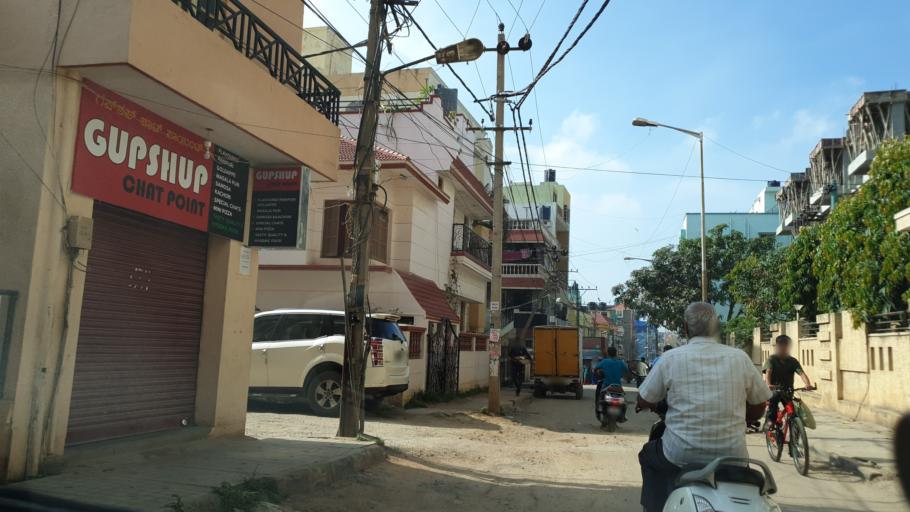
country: IN
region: Karnataka
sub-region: Bangalore Urban
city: Bangalore
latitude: 12.9691
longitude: 77.6703
